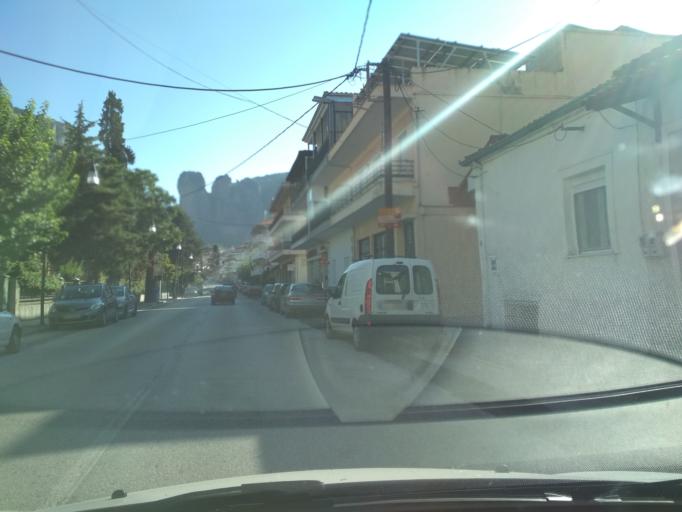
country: GR
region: Thessaly
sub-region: Trikala
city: Kalampaka
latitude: 39.7052
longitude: 21.6190
